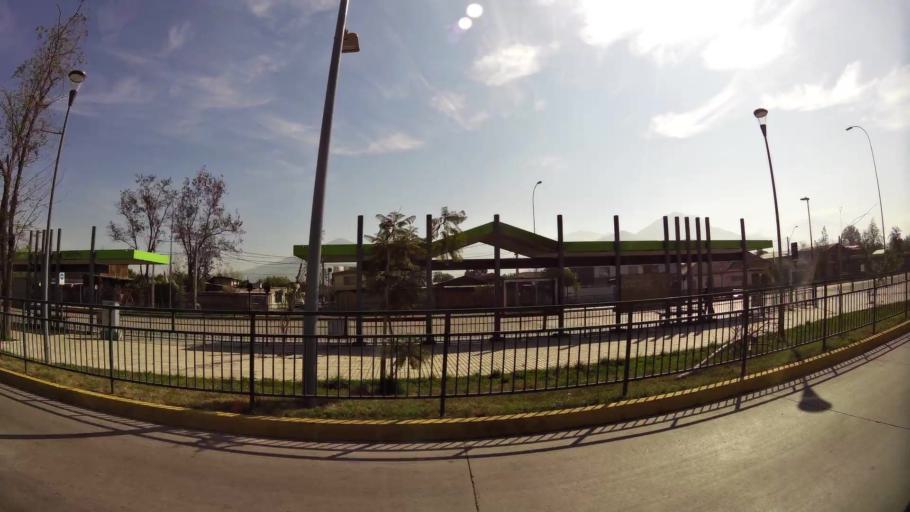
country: CL
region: Santiago Metropolitan
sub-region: Provincia de Santiago
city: Santiago
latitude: -33.3972
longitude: -70.6440
